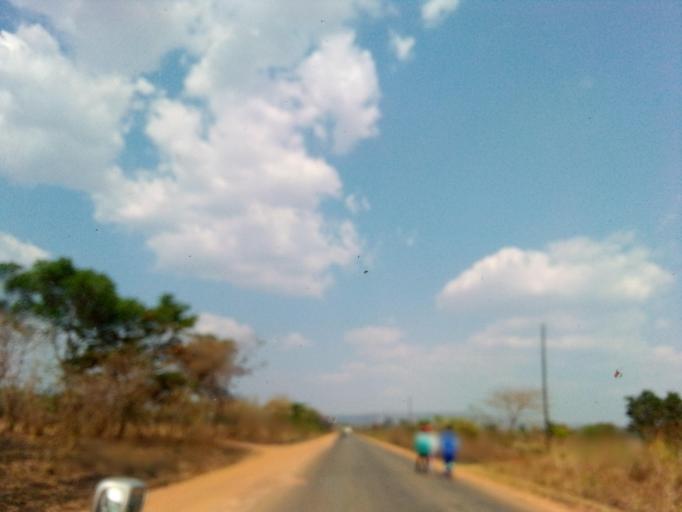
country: ZM
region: Northern
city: Mpika
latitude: -11.8330
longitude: 31.4115
